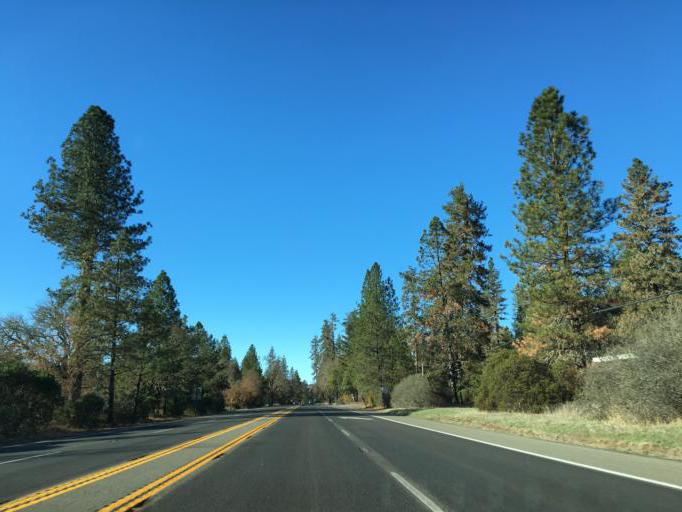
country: US
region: California
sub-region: Mendocino County
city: Laytonville
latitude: 39.7299
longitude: -123.5076
